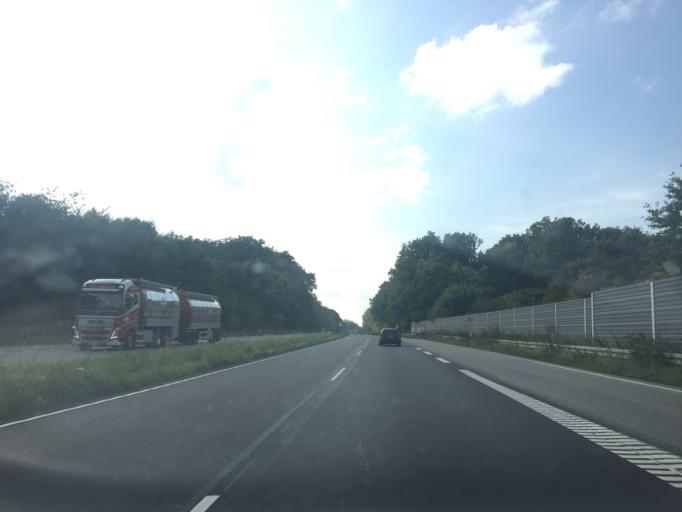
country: DK
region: Zealand
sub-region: Holbaek Kommune
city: Jyderup
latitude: 55.6635
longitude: 11.4051
